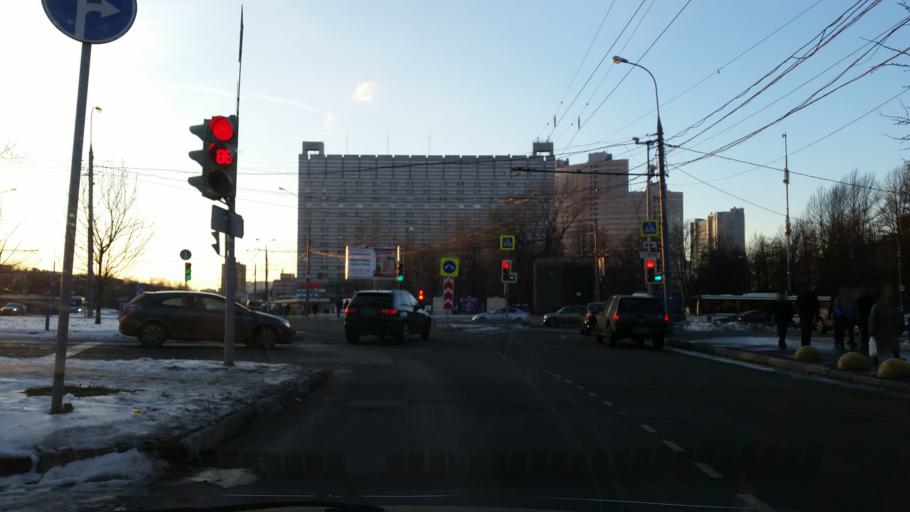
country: RU
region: Moscow
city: Kotlovka
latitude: 55.6533
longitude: 37.5993
